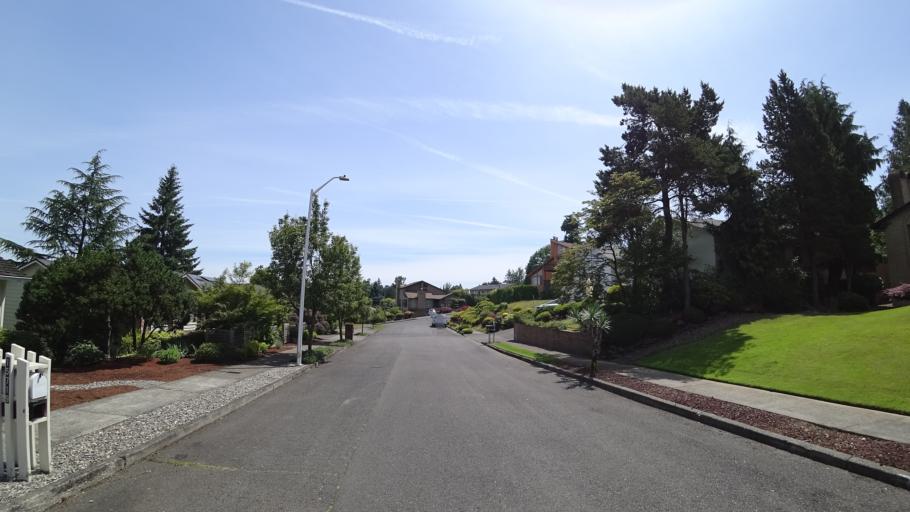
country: US
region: Oregon
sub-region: Multnomah County
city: Fairview
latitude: 45.5458
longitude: -122.5006
